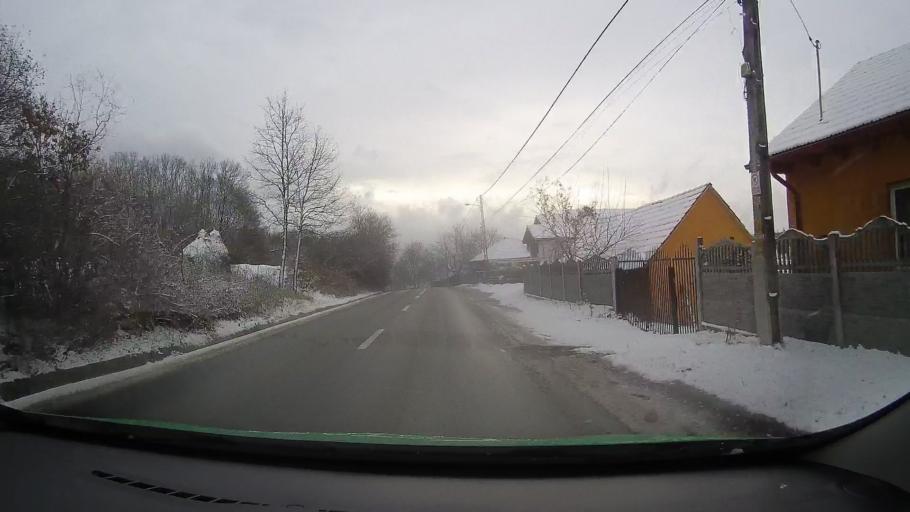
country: RO
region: Hunedoara
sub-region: Oras Hateg
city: Hateg
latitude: 45.6291
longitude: 22.9312
